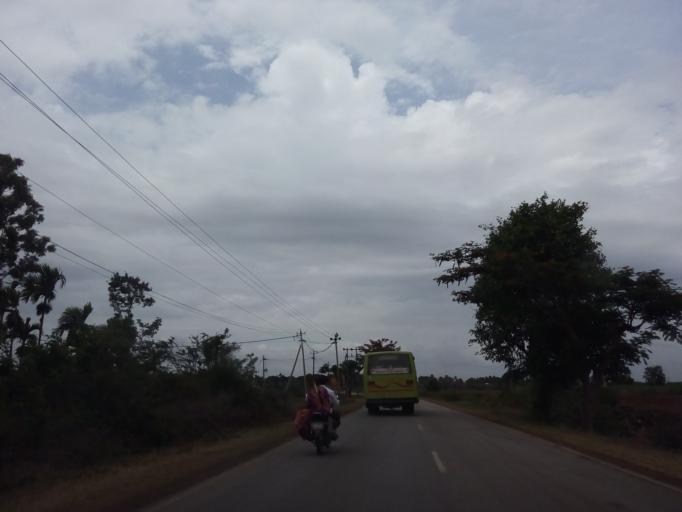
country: IN
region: Karnataka
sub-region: Davanagere
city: Harihar
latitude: 14.5009
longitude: 75.7801
